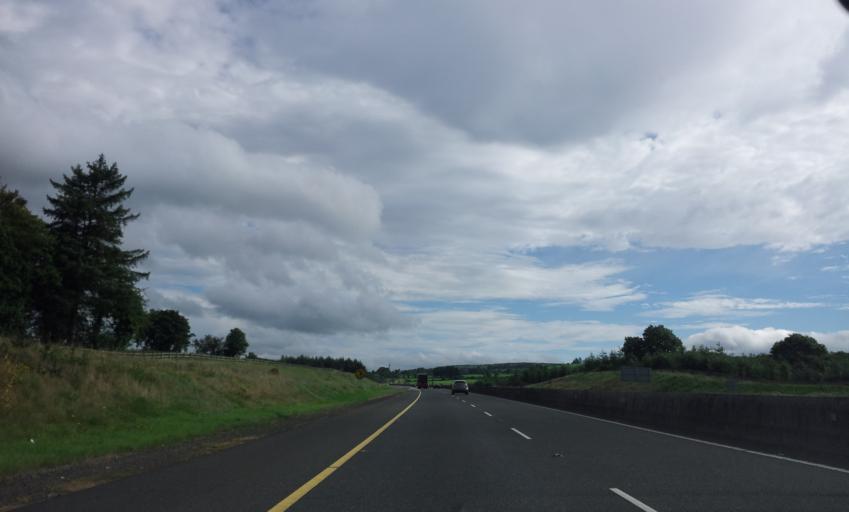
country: IE
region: Munster
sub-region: North Tipperary
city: Newport
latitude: 52.7575
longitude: -8.4073
